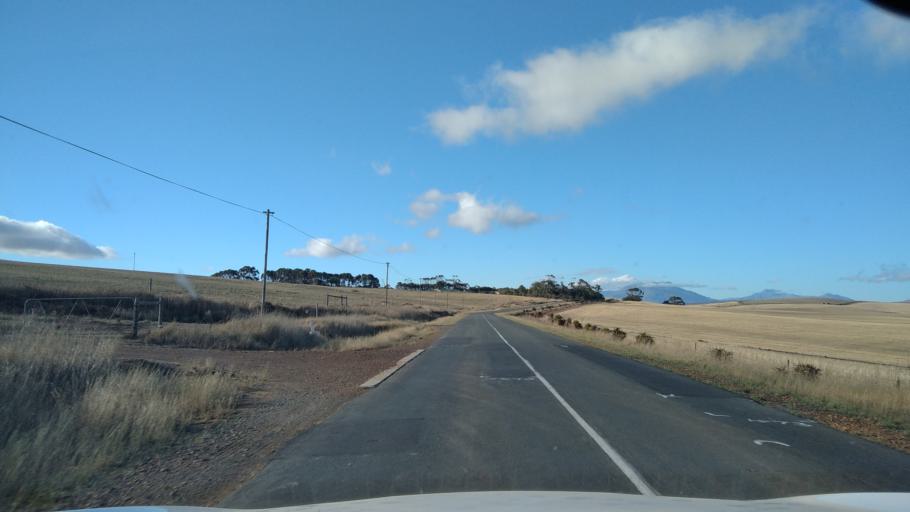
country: ZA
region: Western Cape
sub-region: Overberg District Municipality
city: Caledon
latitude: -34.2075
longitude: 19.2711
